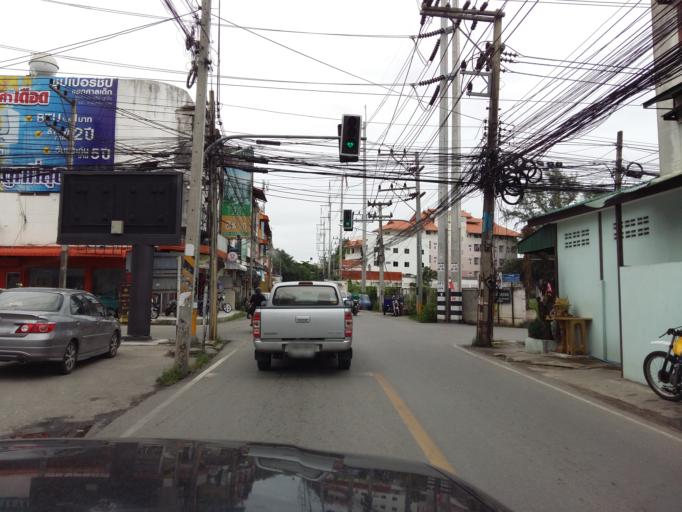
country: TH
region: Chiang Mai
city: Chiang Mai
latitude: 18.7761
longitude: 98.9967
